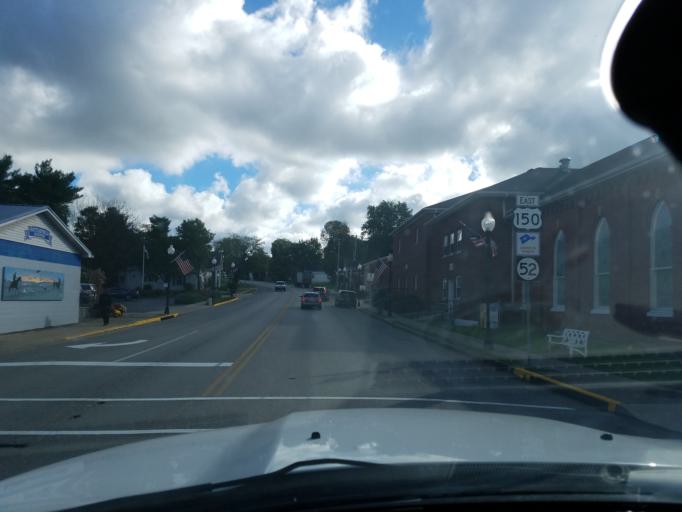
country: US
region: Kentucky
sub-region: Mercer County
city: Harrodsburg
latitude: 37.6504
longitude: -84.9497
